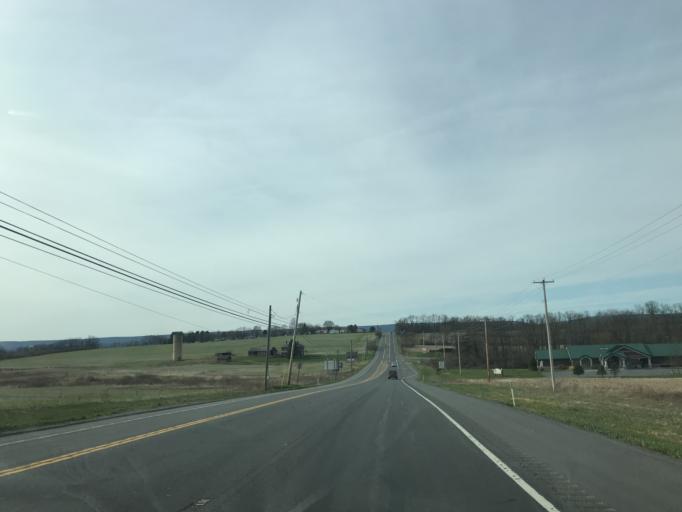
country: US
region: Pennsylvania
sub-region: Northumberland County
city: Dewart
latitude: 41.1155
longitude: -76.9042
